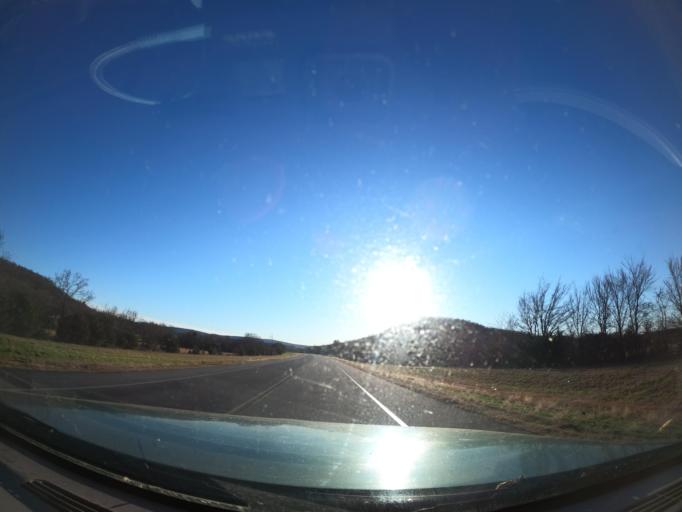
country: US
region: Oklahoma
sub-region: Pittsburg County
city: Hartshorne
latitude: 34.8606
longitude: -95.5298
